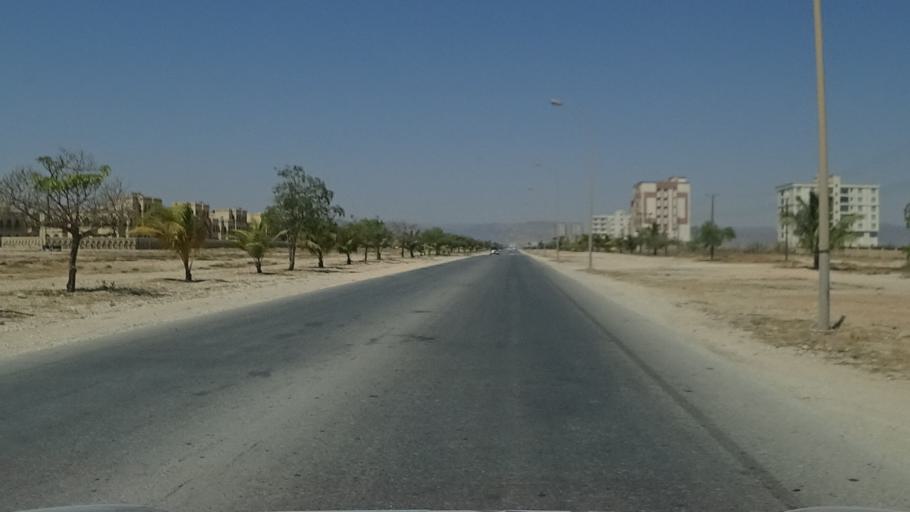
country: OM
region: Zufar
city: Salalah
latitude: 17.0419
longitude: 54.1709
